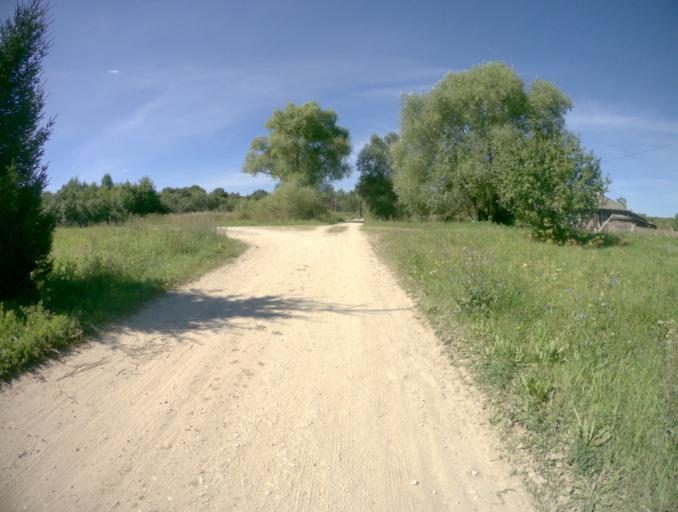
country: RU
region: Vladimir
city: Dobryatino
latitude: 55.6420
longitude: 41.2740
